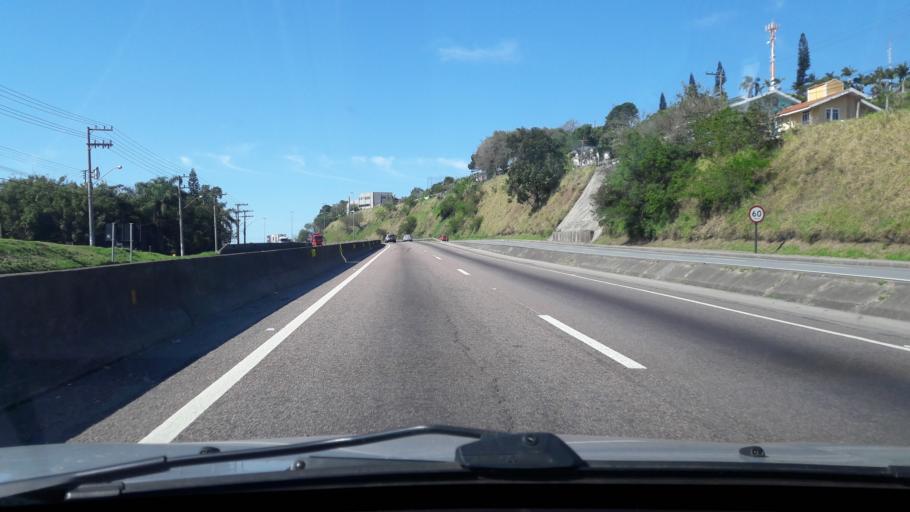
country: BR
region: Santa Catarina
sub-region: Biguacu
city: Biguacu
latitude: -27.5160
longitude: -48.6394
